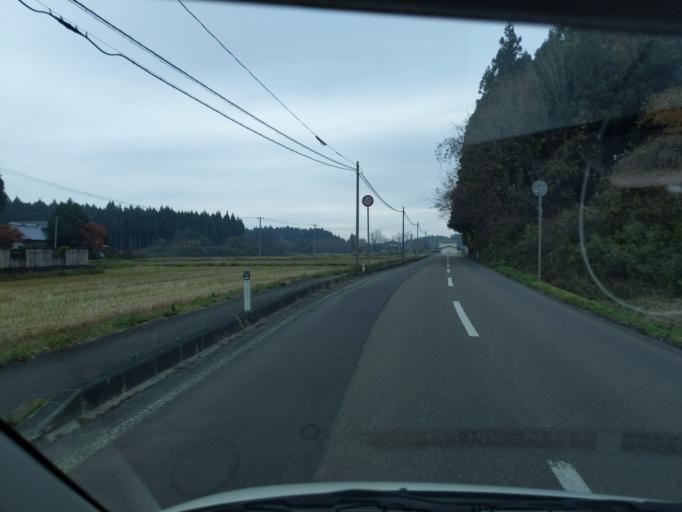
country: JP
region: Iwate
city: Mizusawa
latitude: 39.1029
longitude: 141.0919
